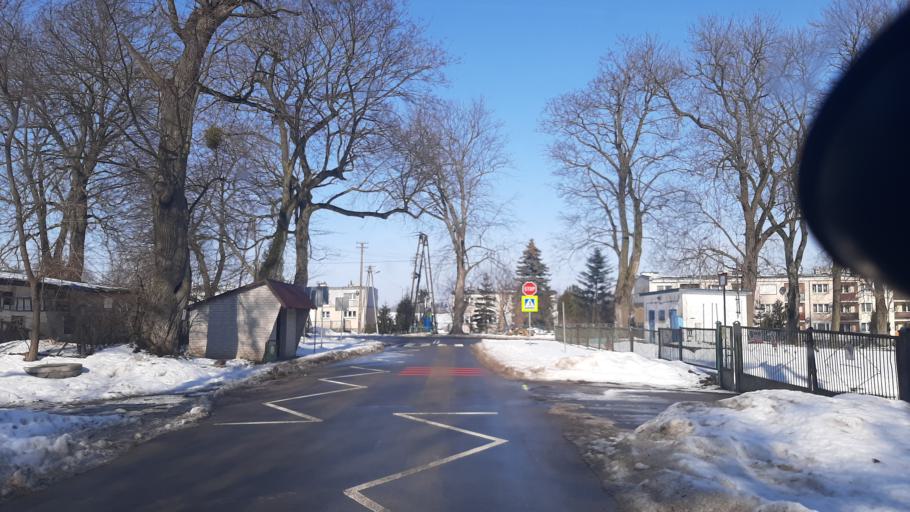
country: PL
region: Lublin Voivodeship
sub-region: Powiat pulawski
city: Naleczow
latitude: 51.3045
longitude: 22.2582
